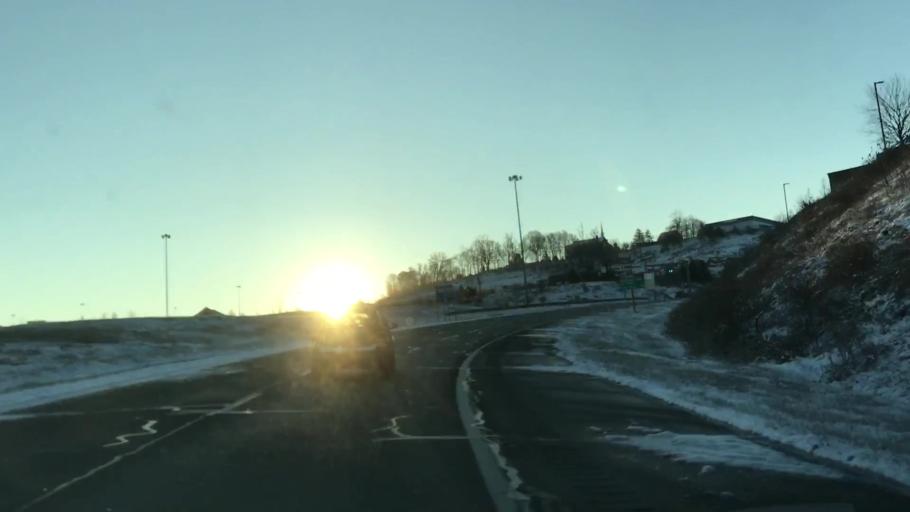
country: US
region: Pennsylvania
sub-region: Allegheny County
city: Oakdale
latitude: 40.4519
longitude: -80.1776
